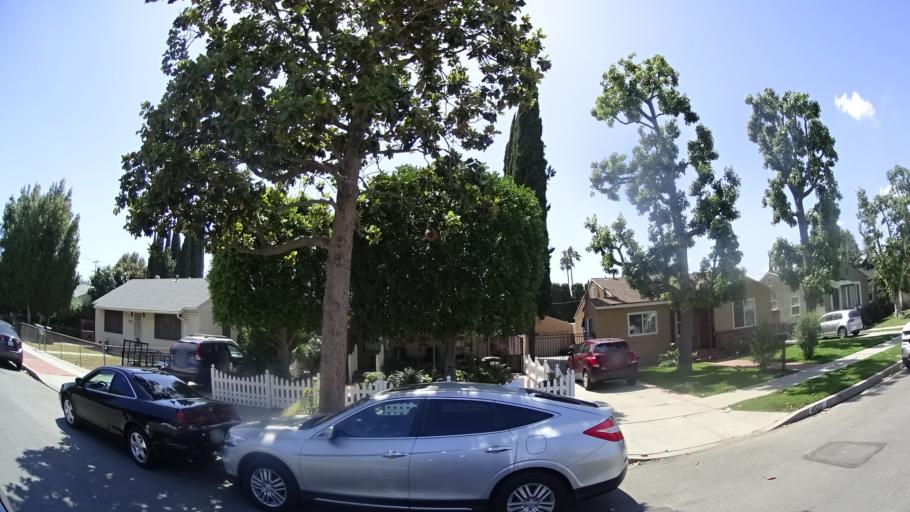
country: US
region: California
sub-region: Los Angeles County
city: Sherman Oaks
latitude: 34.1535
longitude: -118.4422
